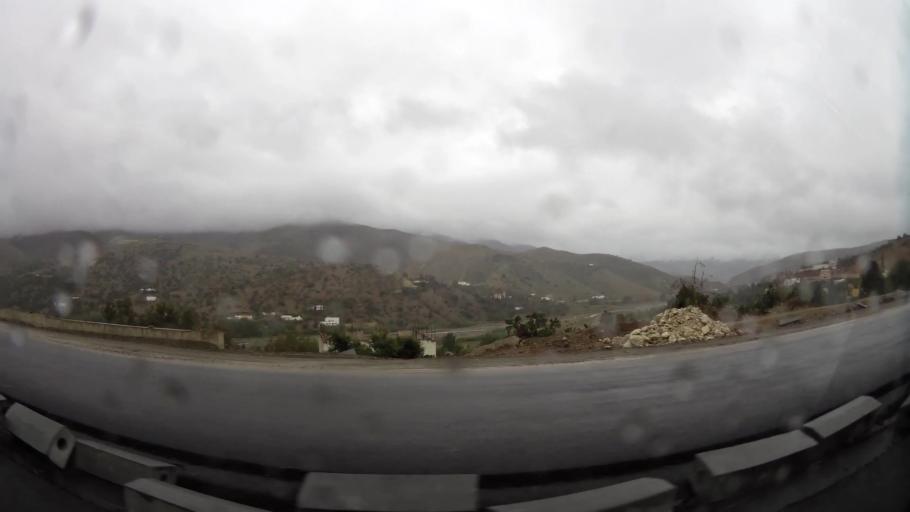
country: MA
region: Taza-Al Hoceima-Taounate
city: Imzourene
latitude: 35.0276
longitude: -3.8217
